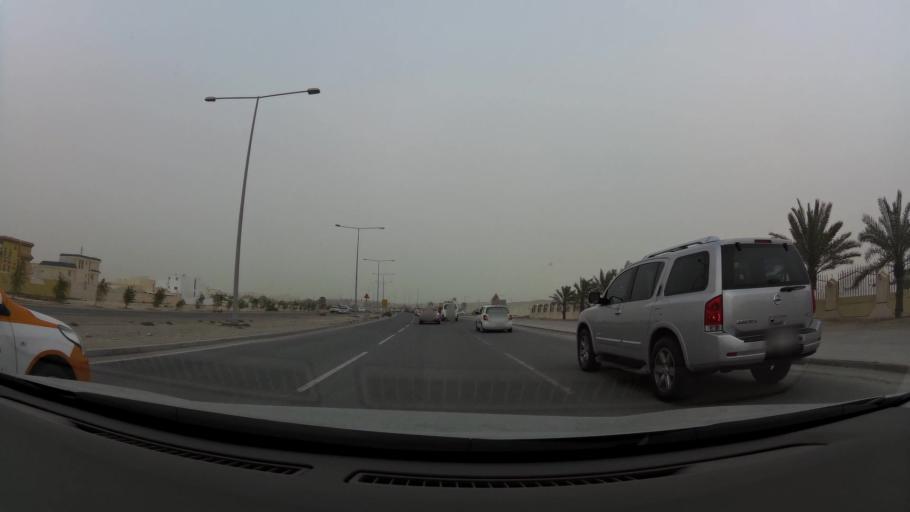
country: QA
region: Baladiyat ad Dawhah
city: Doha
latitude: 25.2271
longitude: 51.4962
